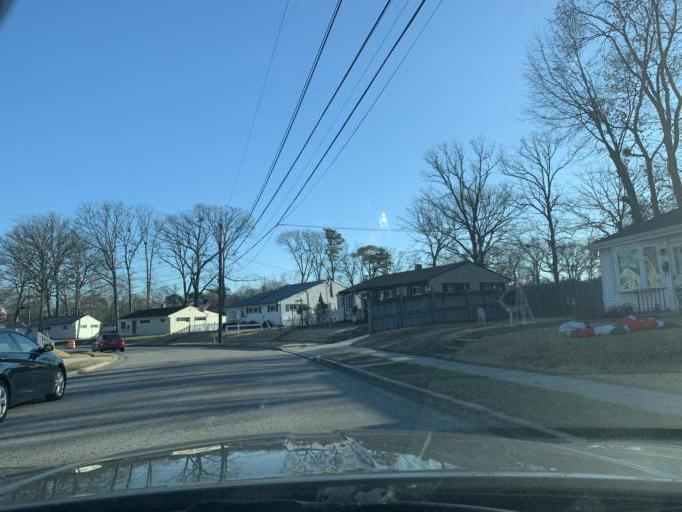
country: US
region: Maryland
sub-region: Anne Arundel County
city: Glen Burnie
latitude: 39.1507
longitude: -76.6293
